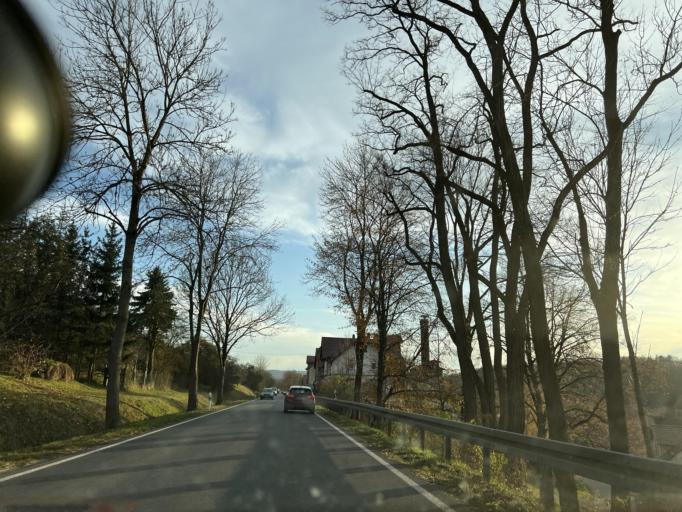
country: DE
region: Thuringia
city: Barchfeld
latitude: 50.8306
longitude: 11.1816
